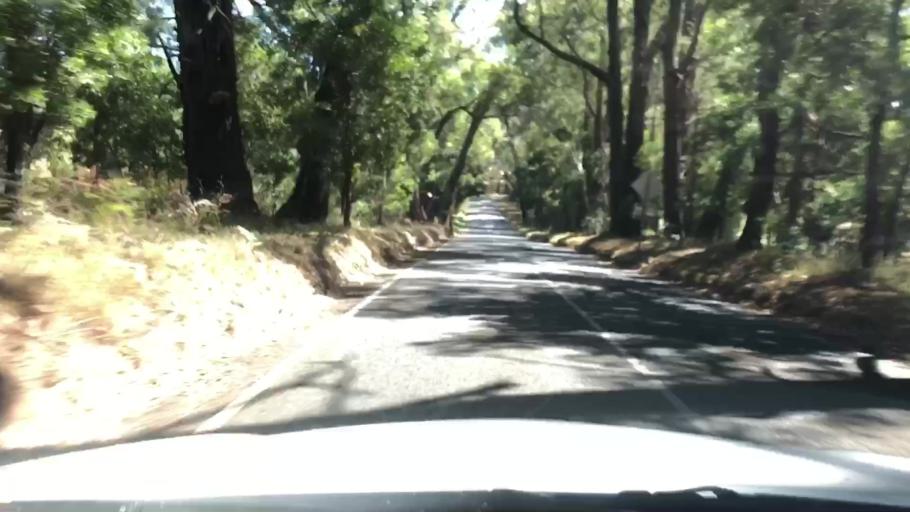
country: AU
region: Victoria
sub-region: Yarra Ranges
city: Macclesfield
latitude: -37.8258
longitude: 145.4925
